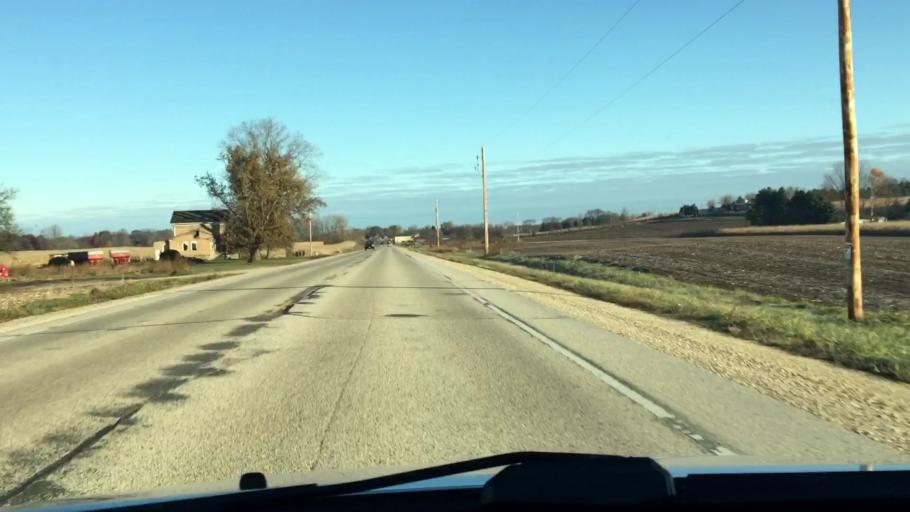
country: US
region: Wisconsin
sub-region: Dodge County
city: Theresa
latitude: 43.4976
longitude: -88.4502
